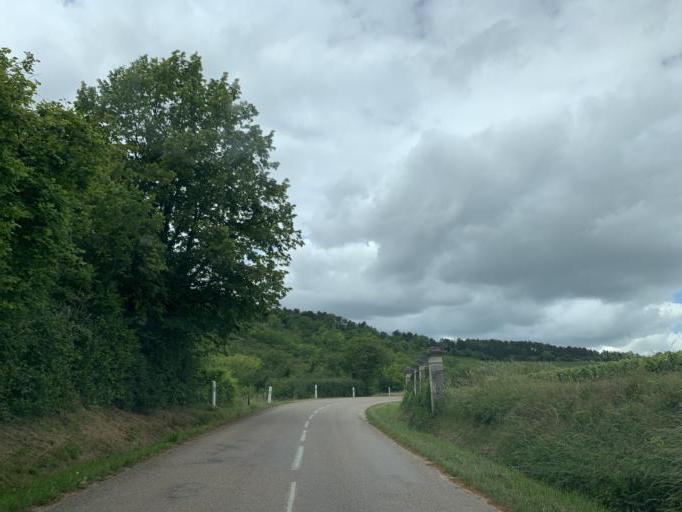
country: FR
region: Bourgogne
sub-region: Departement de l'Yonne
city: Saint-Bris-le-Vineux
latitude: 47.7146
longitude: 3.6718
